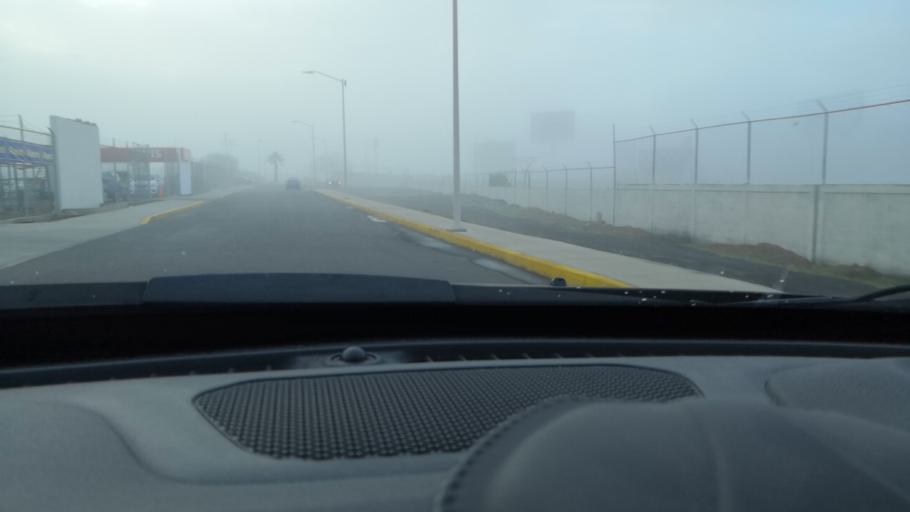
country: MX
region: Guanajuato
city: Colonia Nuevo Mexico
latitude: 20.9846
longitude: -101.4809
